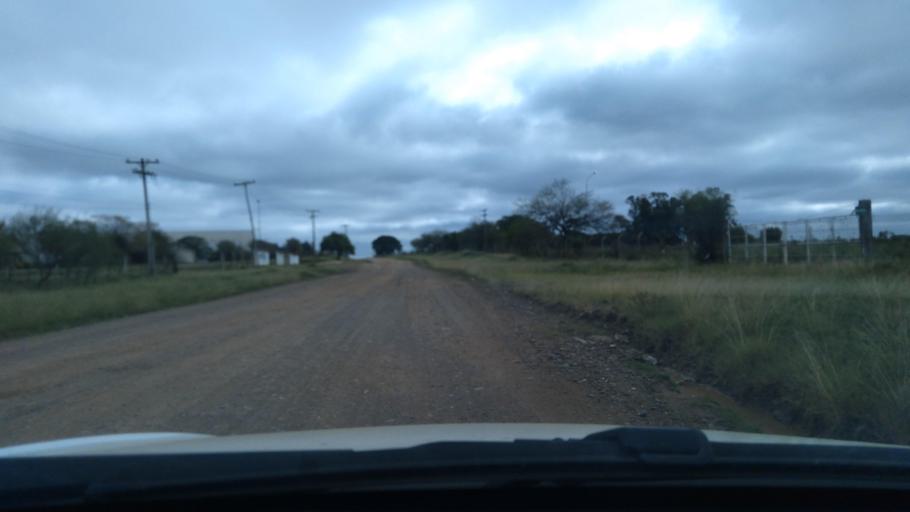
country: BR
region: Rio Grande do Sul
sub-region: Dom Pedrito
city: Dom Pedrito
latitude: -30.9835
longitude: -54.6410
